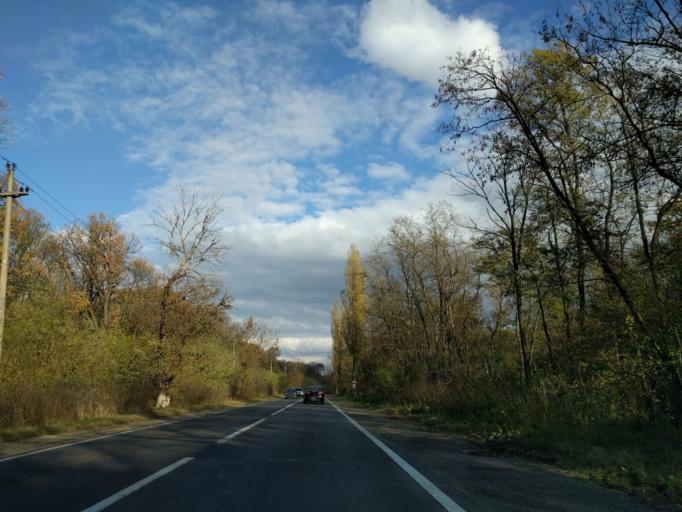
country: RO
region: Ilfov
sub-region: Comuna Ganeasa
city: Ganeasa
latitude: 44.4576
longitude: 26.2989
